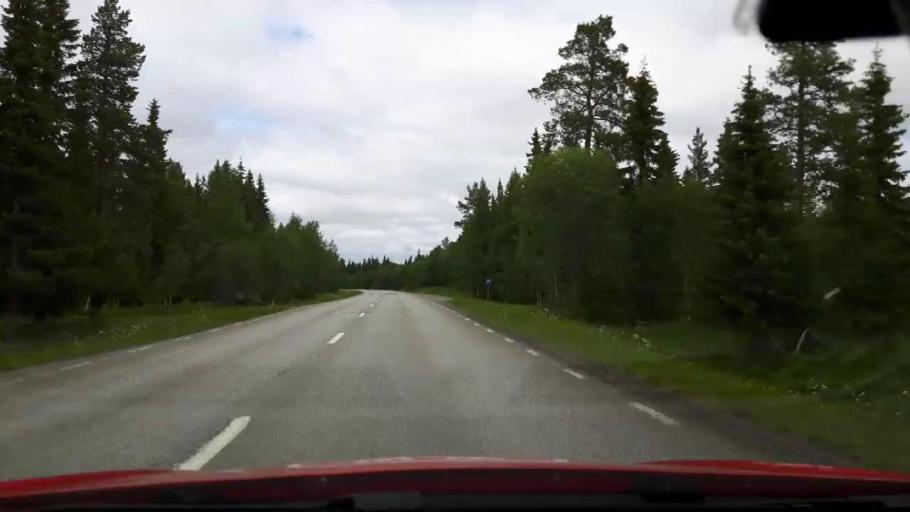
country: SE
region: Jaemtland
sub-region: Krokoms Kommun
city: Krokom
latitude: 63.4286
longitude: 14.4981
